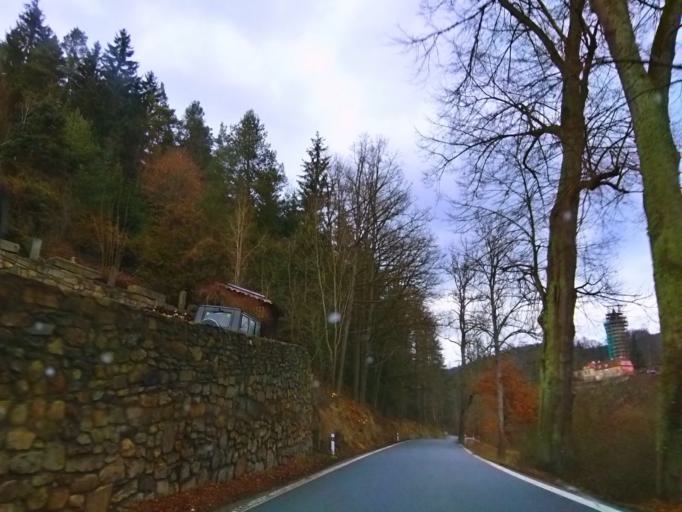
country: CZ
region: Jihocesky
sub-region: Okres Cesky Krumlov
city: Vyssi Brod
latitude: 48.6551
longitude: 14.3615
